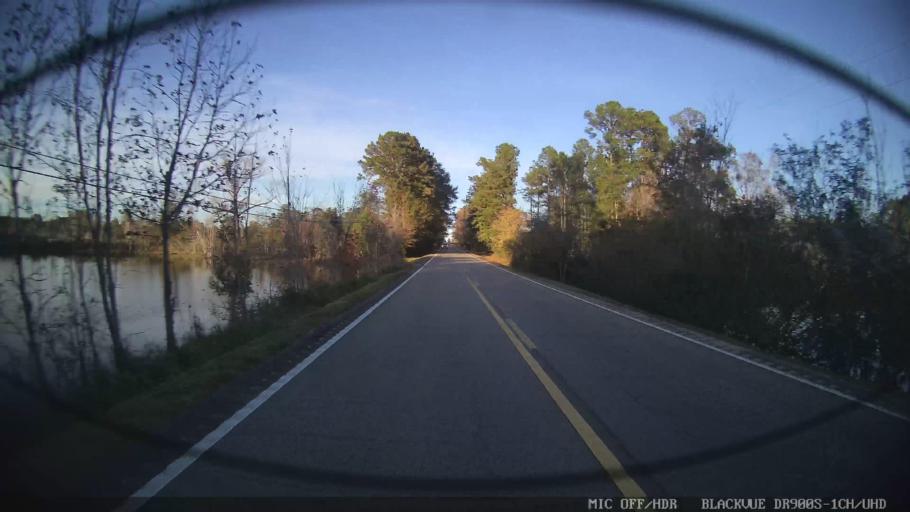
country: US
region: Mississippi
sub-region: Lamar County
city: Lumberton
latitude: 31.0339
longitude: -89.4424
